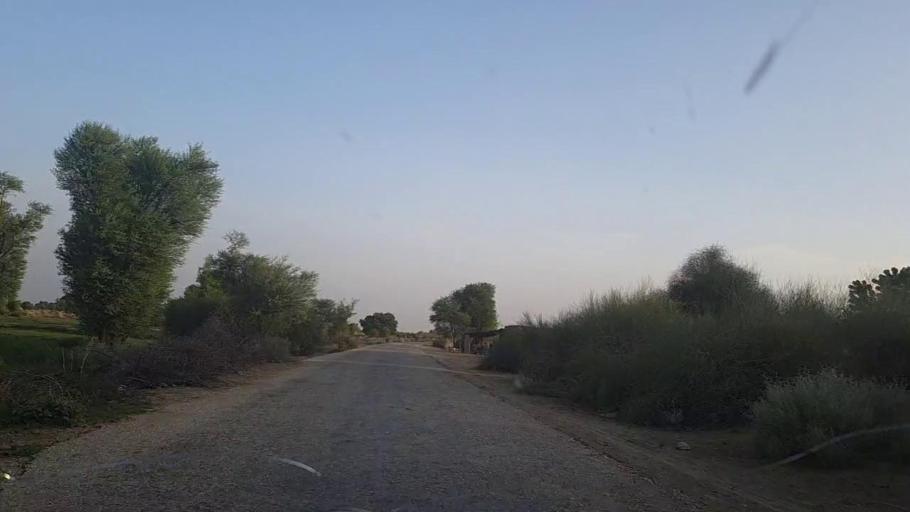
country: PK
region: Sindh
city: Khanpur
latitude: 27.6228
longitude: 69.4449
